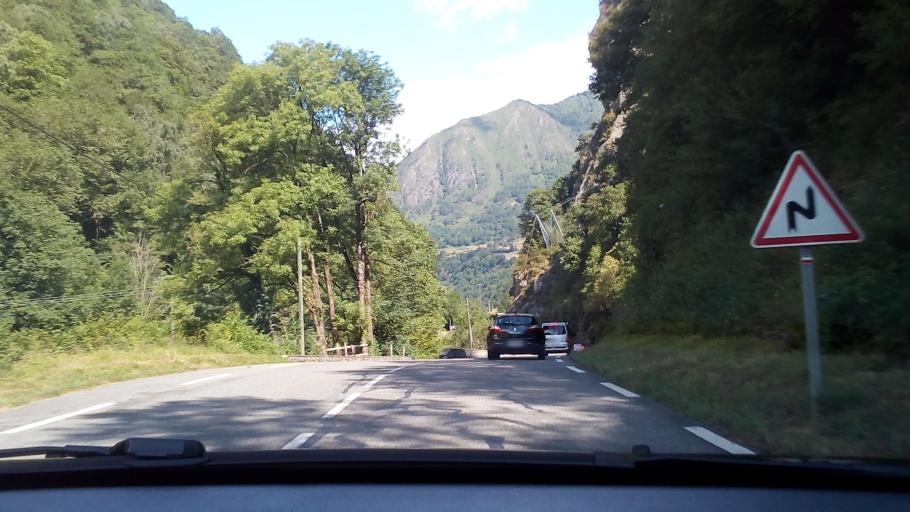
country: FR
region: Aquitaine
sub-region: Departement des Pyrenees-Atlantiques
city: Laruns
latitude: 42.9206
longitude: -0.5774
